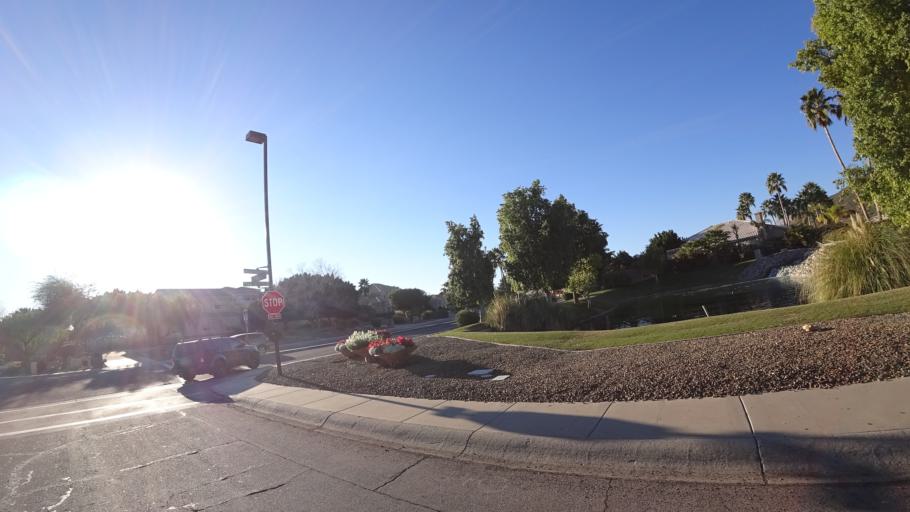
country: US
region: Arizona
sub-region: Maricopa County
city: Peoria
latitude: 33.6818
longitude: -112.1916
